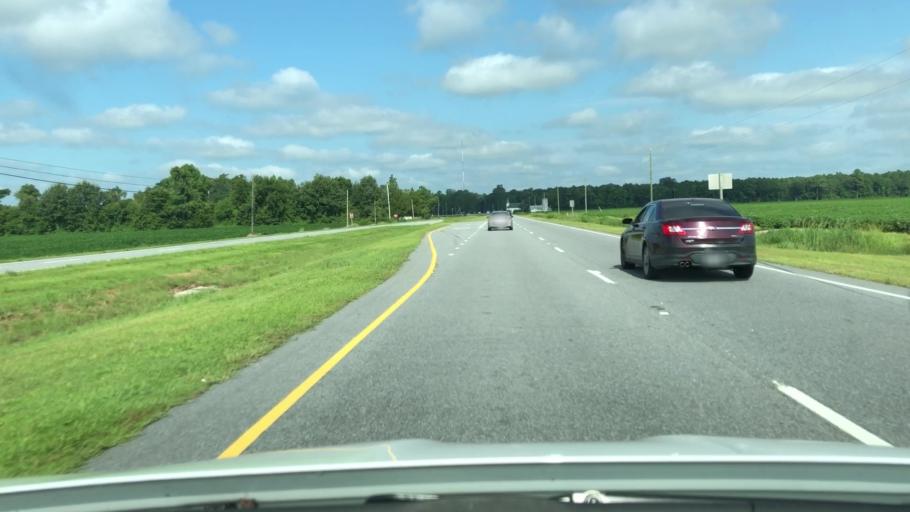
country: US
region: North Carolina
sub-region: Perquimans County
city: Hertford
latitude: 36.2106
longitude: -76.4225
